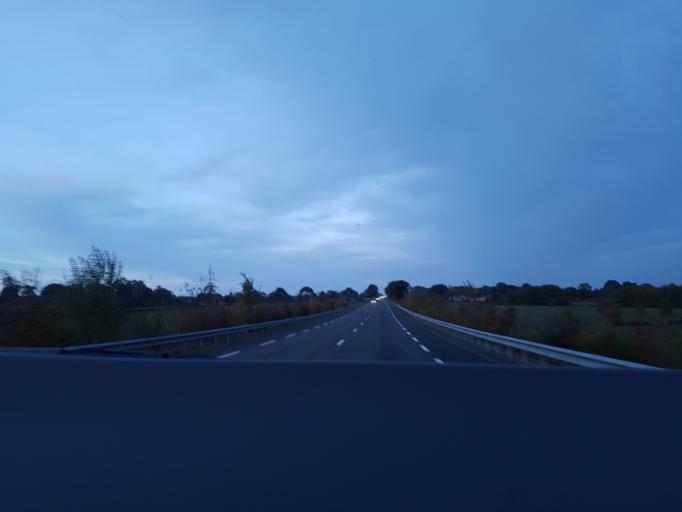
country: FR
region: Pays de la Loire
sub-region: Departement de la Mayenne
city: Montigne-le-Brillant
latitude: 48.0085
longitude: -0.8336
